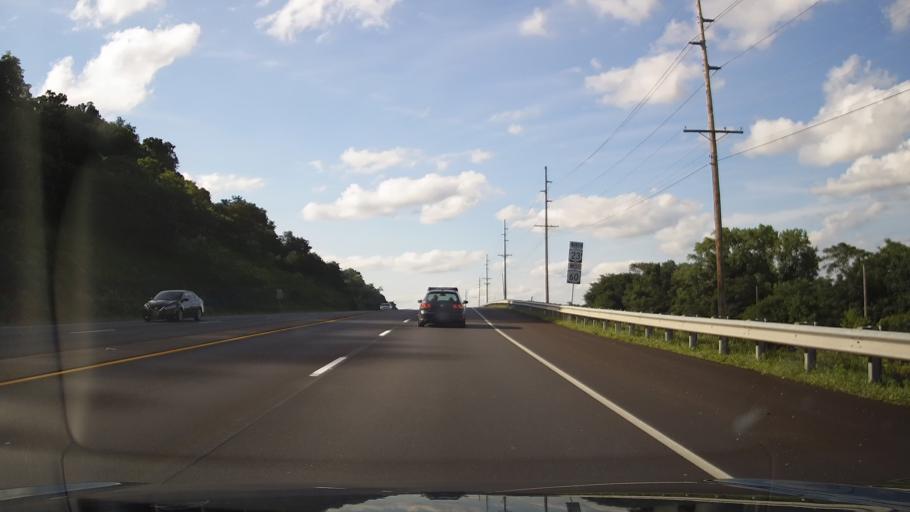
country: US
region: Ohio
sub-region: Lawrence County
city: South Point
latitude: 38.4222
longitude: -82.6016
